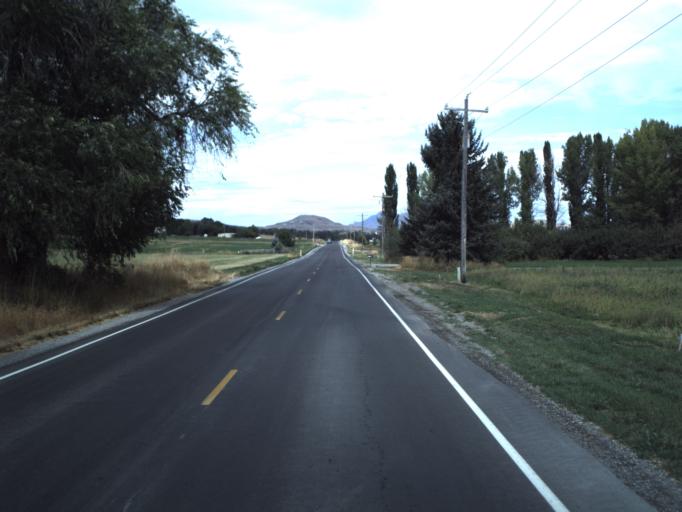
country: US
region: Utah
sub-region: Cache County
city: Mendon
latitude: 41.6819
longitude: -111.9625
